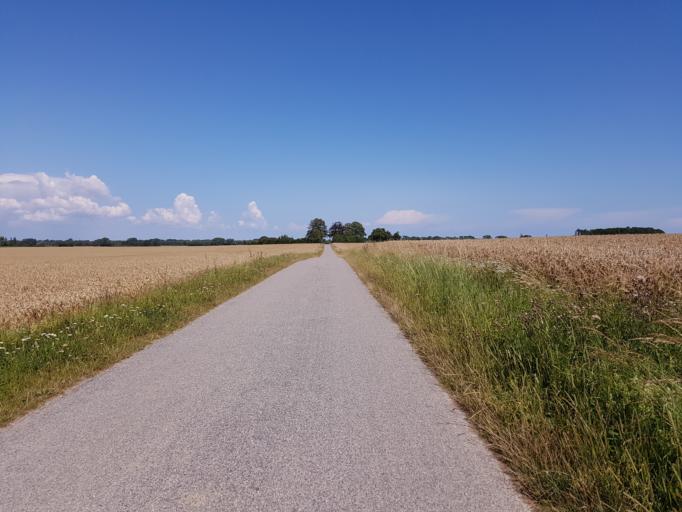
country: DK
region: Zealand
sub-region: Guldborgsund Kommune
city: Nykobing Falster
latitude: 54.5748
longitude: 11.9546
